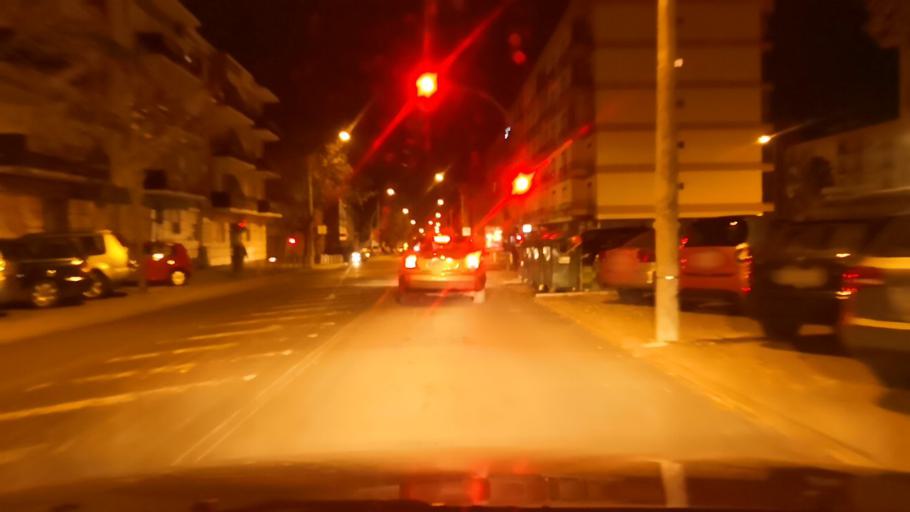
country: PT
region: Setubal
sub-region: Setubal
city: Setubal
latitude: 38.5375
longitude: -8.8944
